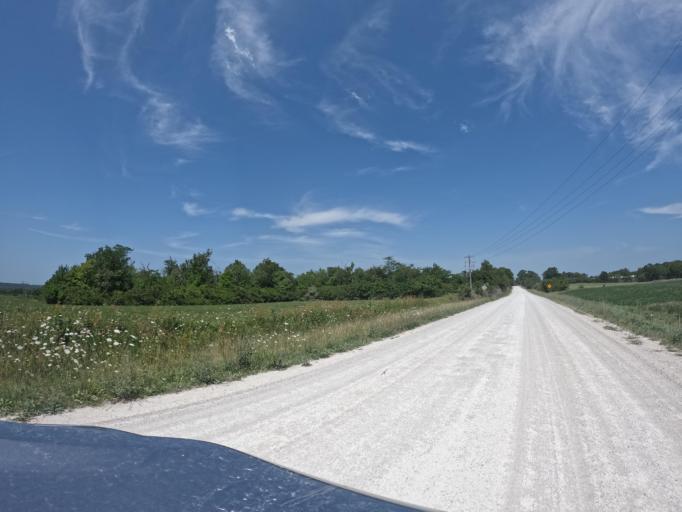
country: US
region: Iowa
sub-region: Henry County
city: Mount Pleasant
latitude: 40.9061
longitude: -91.5469
